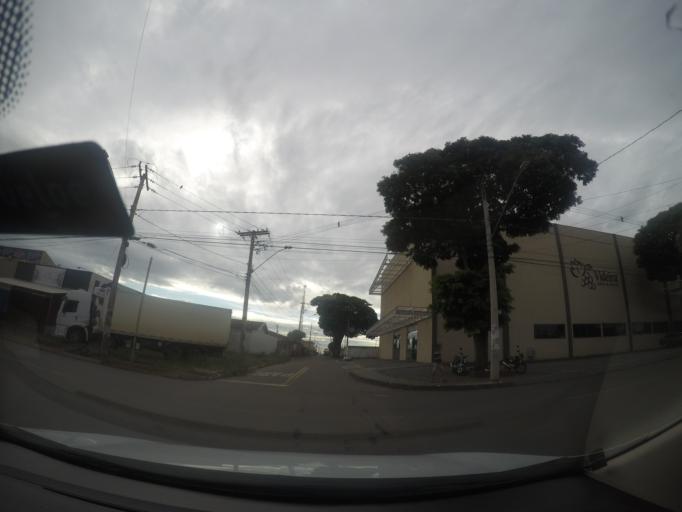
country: BR
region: Goias
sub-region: Goiania
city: Goiania
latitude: -16.6096
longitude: -49.3182
